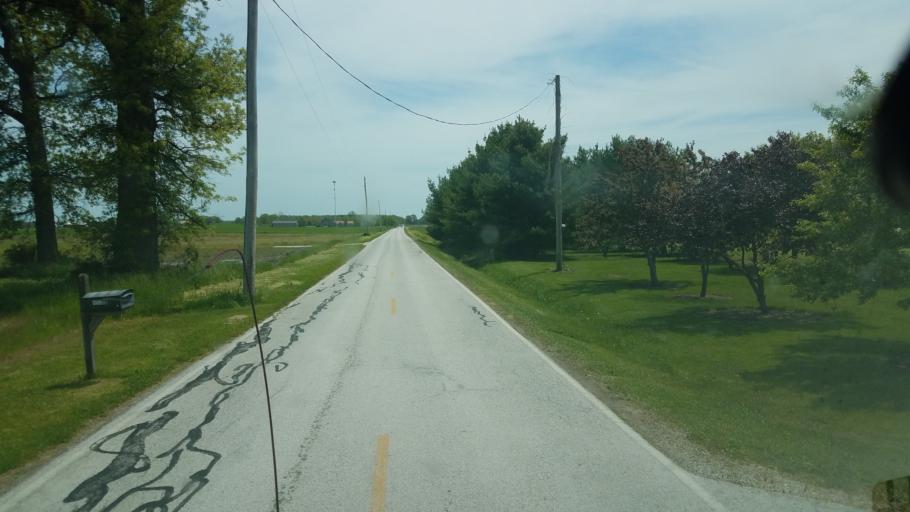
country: US
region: Ohio
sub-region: Ottawa County
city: Oak Harbor
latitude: 41.4869
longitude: -83.1622
